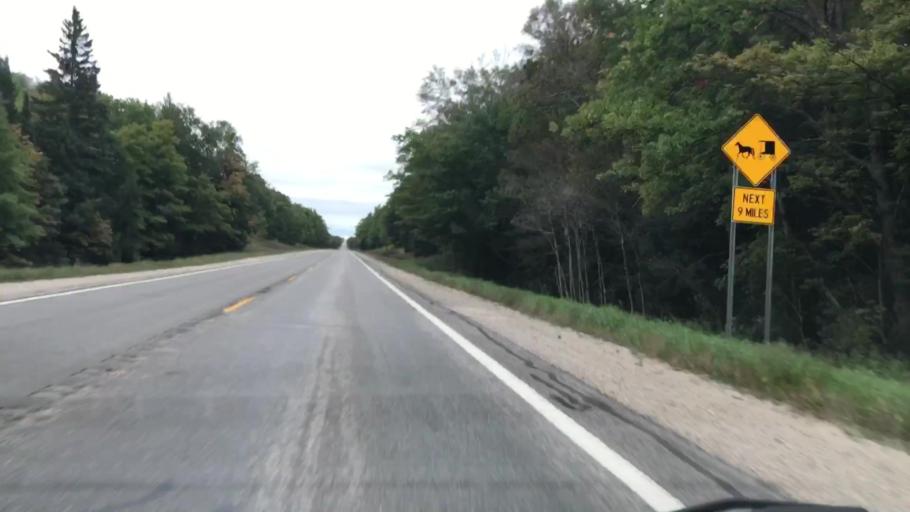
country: US
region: Michigan
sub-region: Luce County
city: Newberry
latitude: 46.2450
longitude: -85.5723
